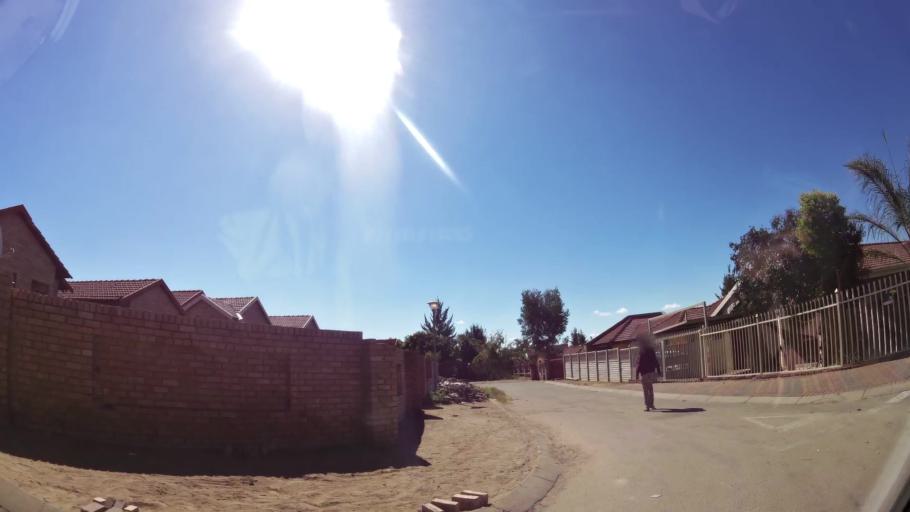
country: ZA
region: Limpopo
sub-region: Capricorn District Municipality
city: Polokwane
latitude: -23.8702
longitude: 29.4312
